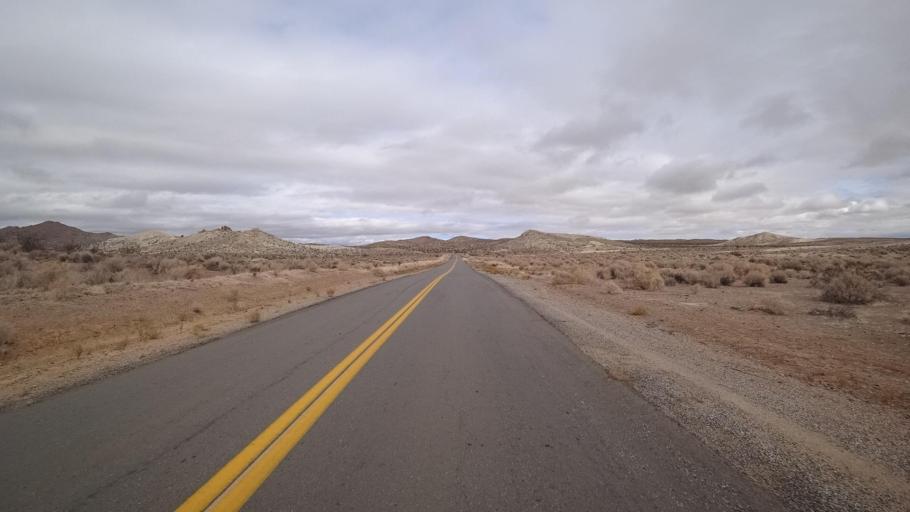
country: US
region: California
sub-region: Kern County
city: Rosamond
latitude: 34.9017
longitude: -118.2162
